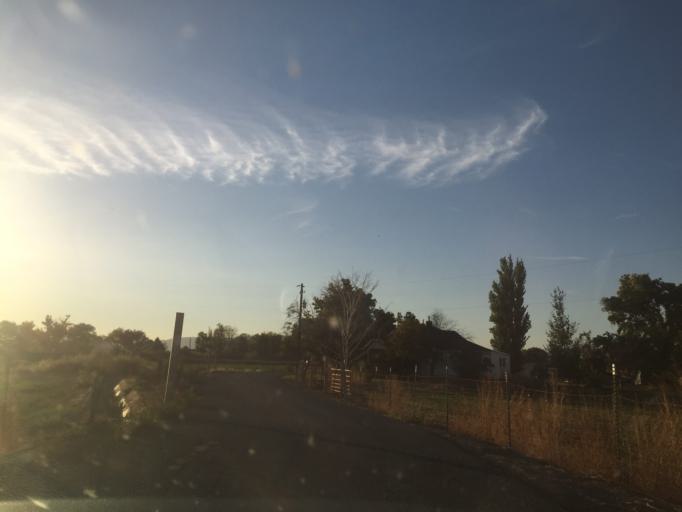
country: US
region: Utah
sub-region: Utah County
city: Benjamin
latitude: 40.1521
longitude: -111.7258
